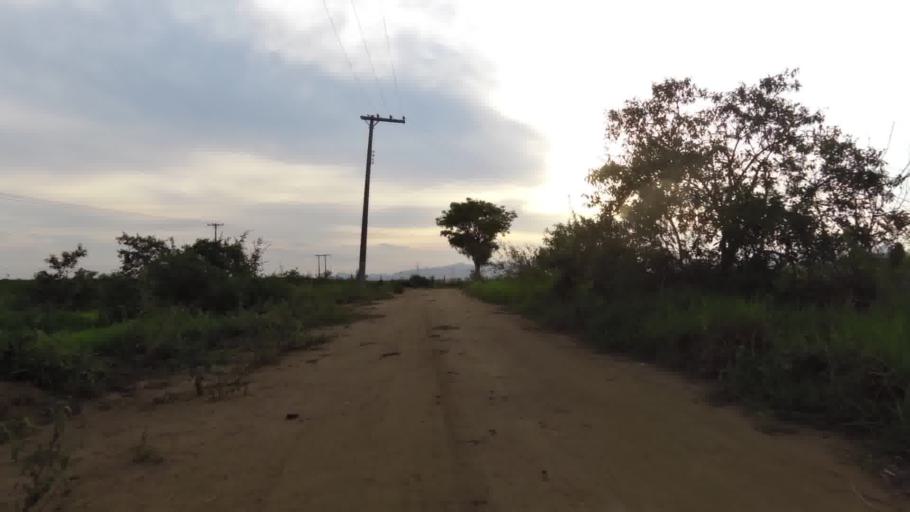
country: BR
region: Espirito Santo
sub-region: Piuma
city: Piuma
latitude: -20.8298
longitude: -40.7342
